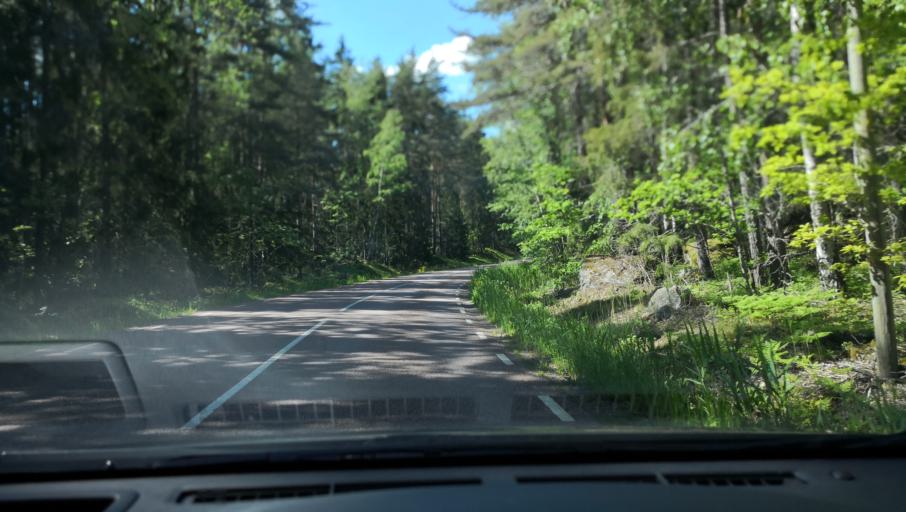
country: SE
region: Vaestmanland
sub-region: Arboga Kommun
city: Tyringe
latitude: 59.2957
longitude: 16.0342
